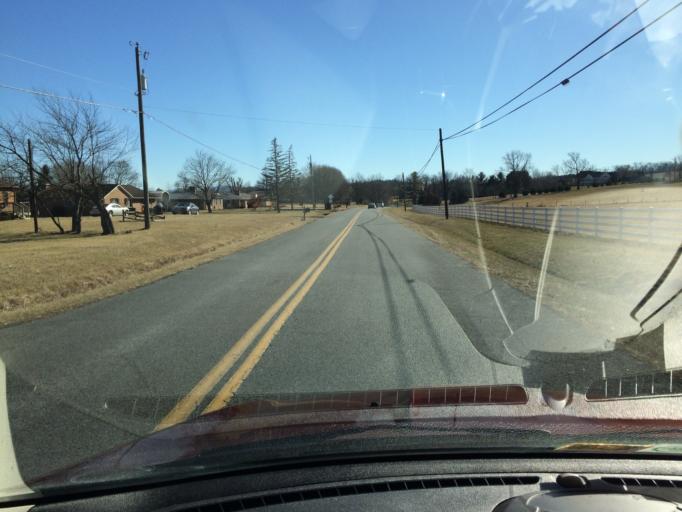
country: US
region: Virginia
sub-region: Rockingham County
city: Bridgewater
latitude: 38.3699
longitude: -78.9786
